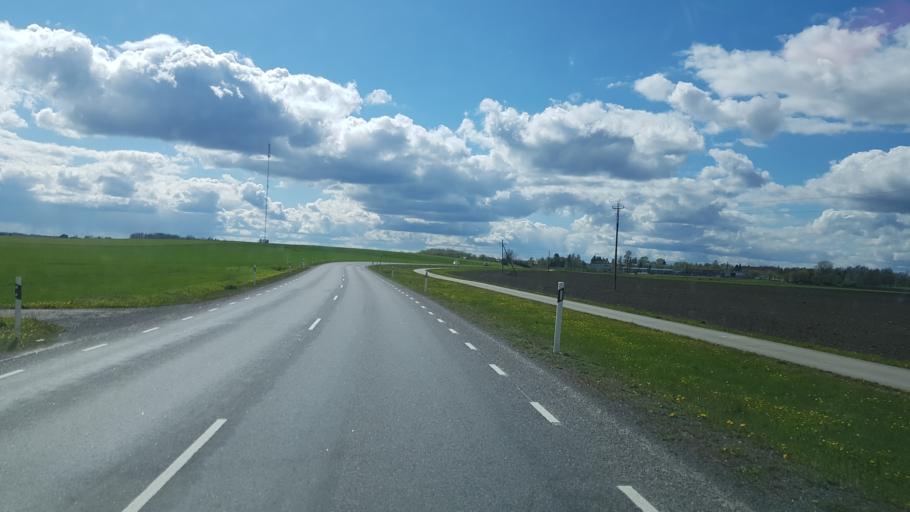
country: EE
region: Jaervamaa
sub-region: Tueri vald
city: Sarevere
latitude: 58.7799
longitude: 25.4508
